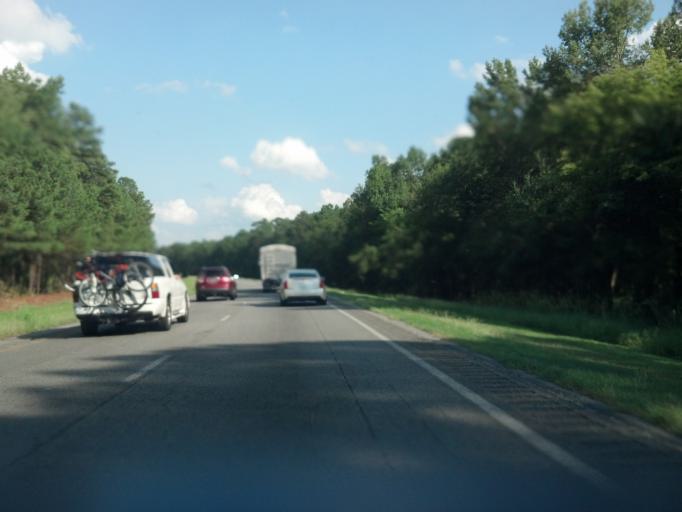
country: US
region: North Carolina
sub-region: Nash County
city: Rocky Mount
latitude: 35.9377
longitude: -77.7519
